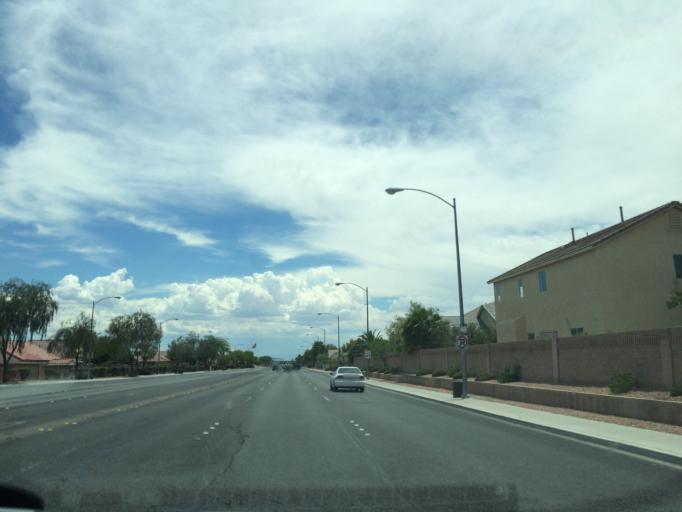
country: US
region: Nevada
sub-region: Clark County
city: North Las Vegas
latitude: 36.2690
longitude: -115.1800
